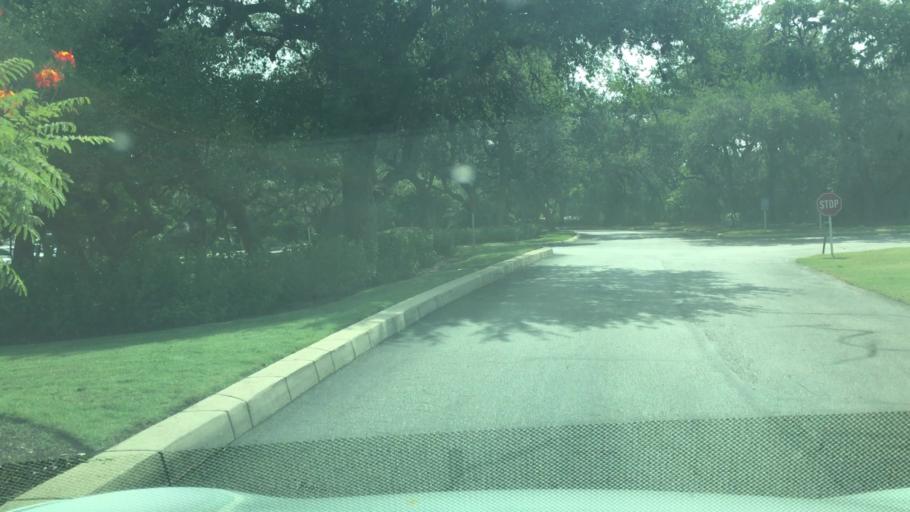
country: US
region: Texas
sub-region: Bexar County
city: Leon Valley
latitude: 29.4606
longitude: -98.6838
